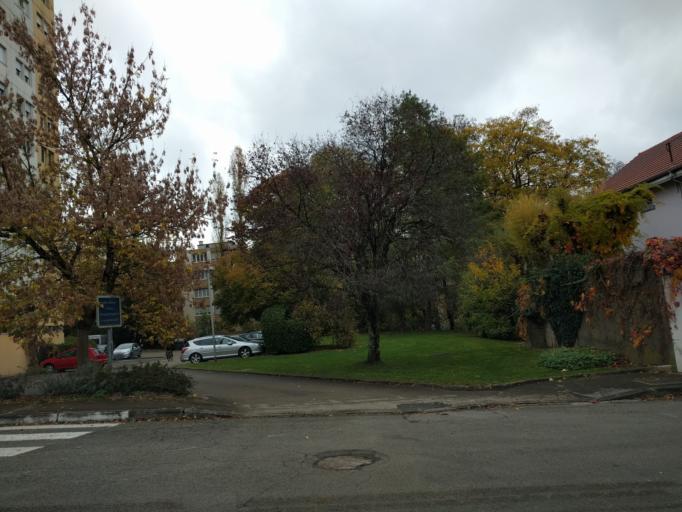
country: FR
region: Franche-Comte
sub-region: Departement du Doubs
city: Besancon
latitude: 47.2512
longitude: 6.0236
